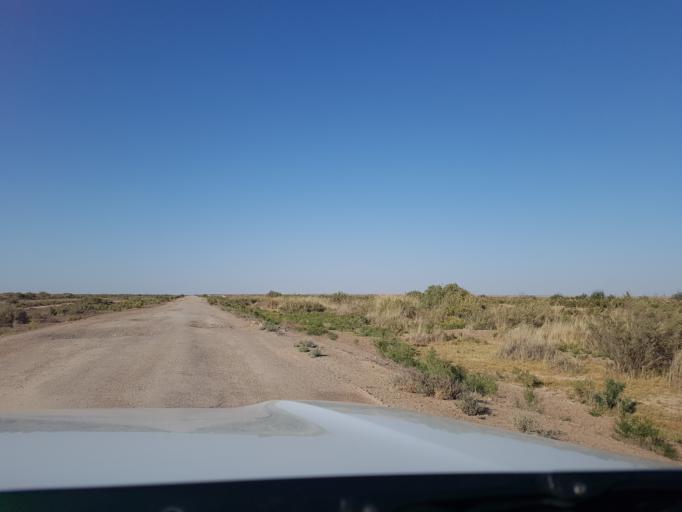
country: IR
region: Razavi Khorasan
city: Sarakhs
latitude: 36.9628
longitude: 61.3825
